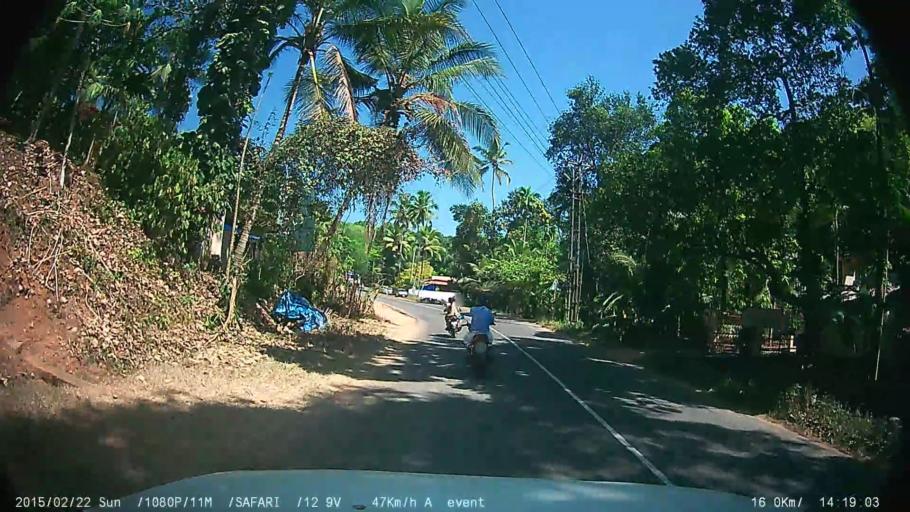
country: IN
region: Kerala
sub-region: Kottayam
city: Lalam
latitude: 9.5674
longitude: 76.6890
